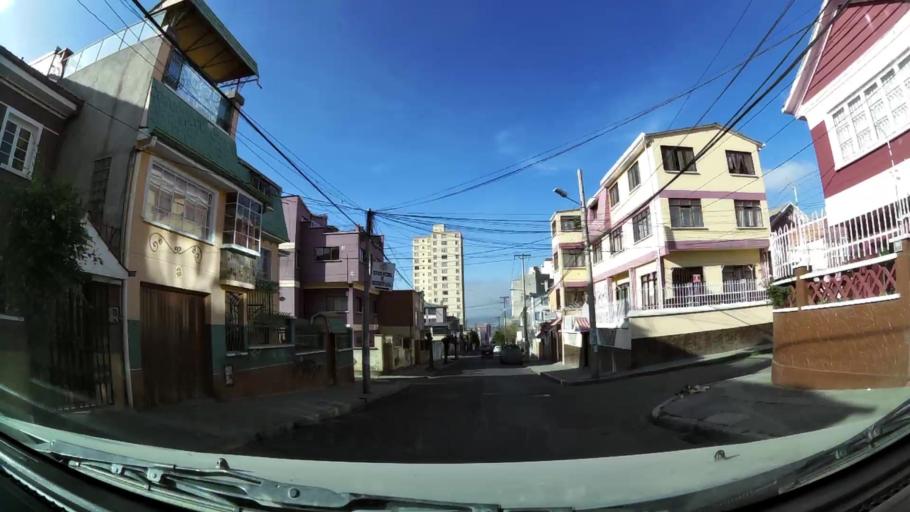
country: BO
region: La Paz
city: La Paz
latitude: -16.4939
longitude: -68.1204
